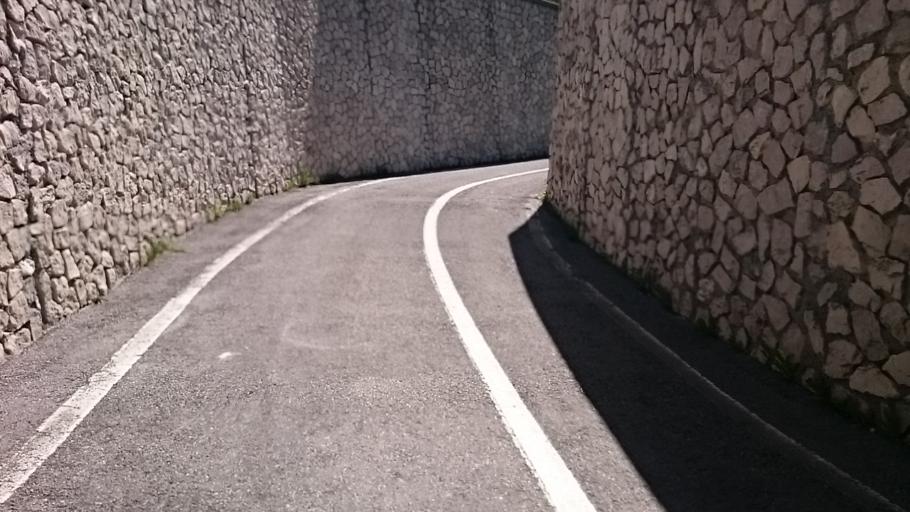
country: IT
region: Veneto
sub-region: Provincia di Belluno
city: San Vito
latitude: 46.4794
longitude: 12.1961
